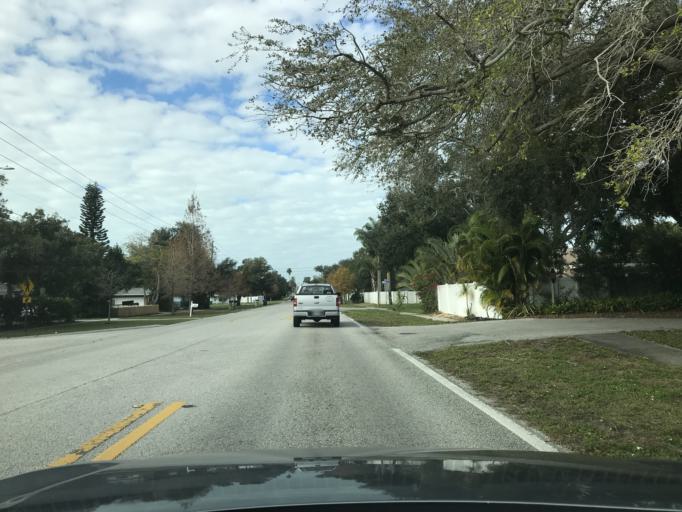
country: US
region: Florida
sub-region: Pinellas County
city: Largo
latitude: 27.9277
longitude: -82.7762
